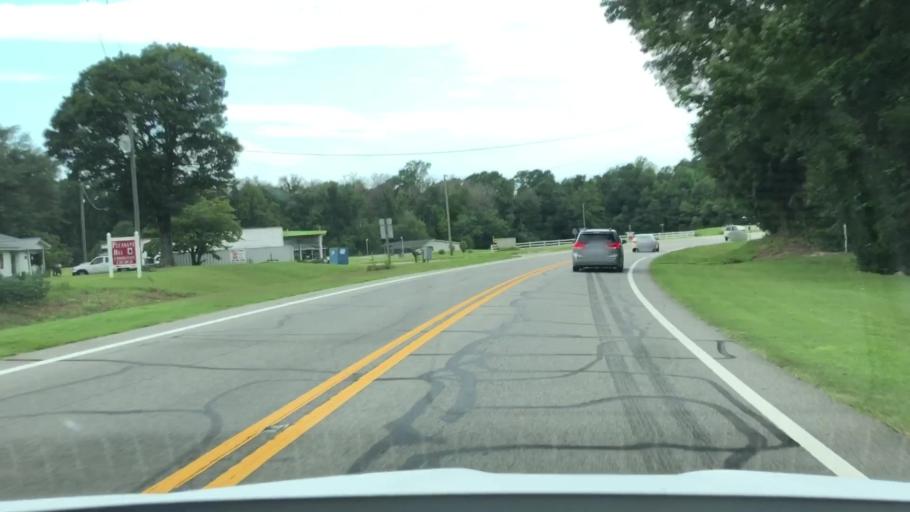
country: US
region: North Carolina
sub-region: Lenoir County
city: Kinston
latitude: 35.1568
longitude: -77.5523
